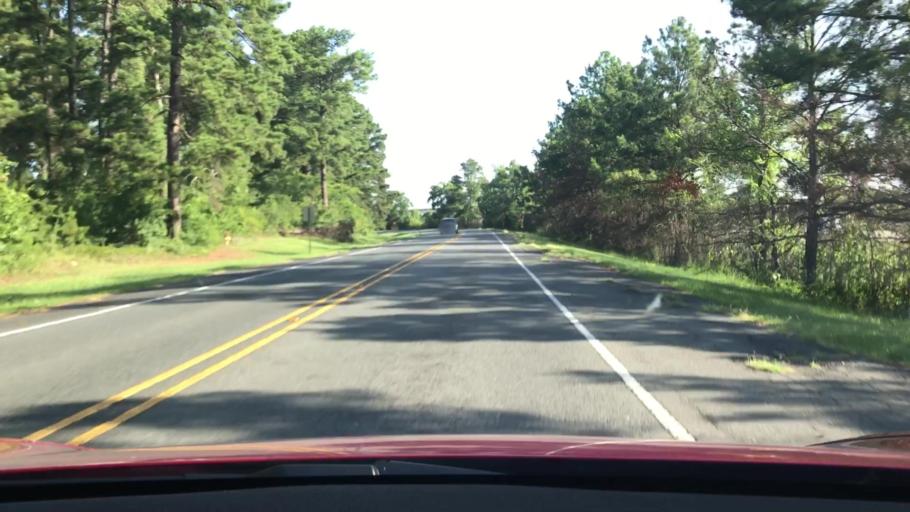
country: US
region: Louisiana
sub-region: Caddo Parish
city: Shreveport
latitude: 32.4513
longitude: -93.8439
